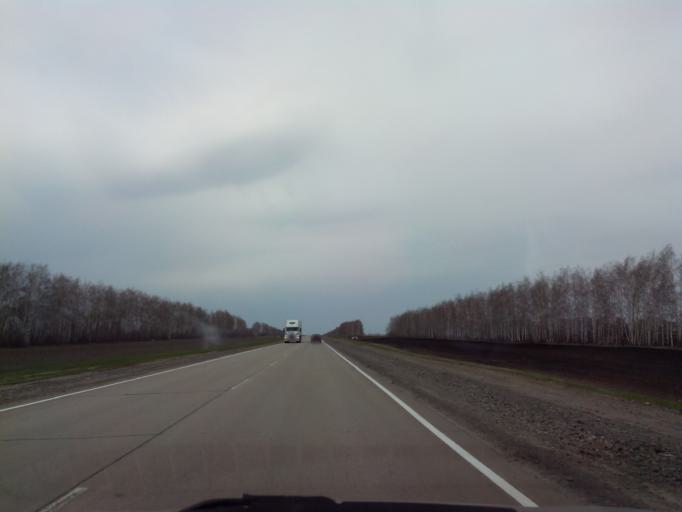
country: RU
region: Tambov
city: Znamenka
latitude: 52.2586
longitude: 41.5084
